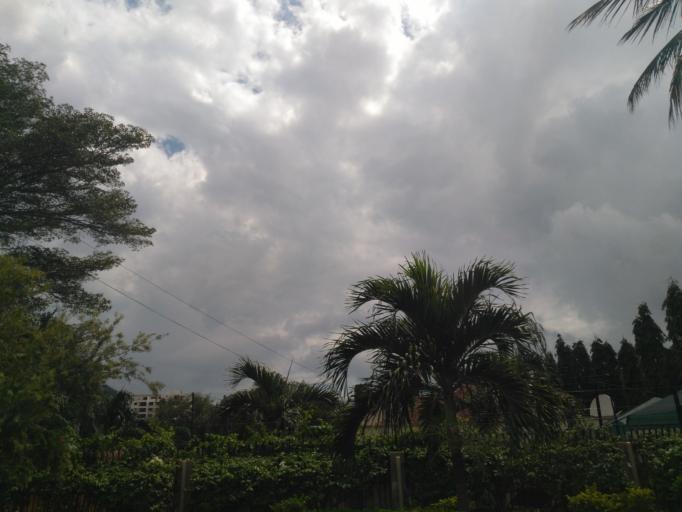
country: TZ
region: Dar es Salaam
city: Magomeni
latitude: -6.7589
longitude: 39.2468
